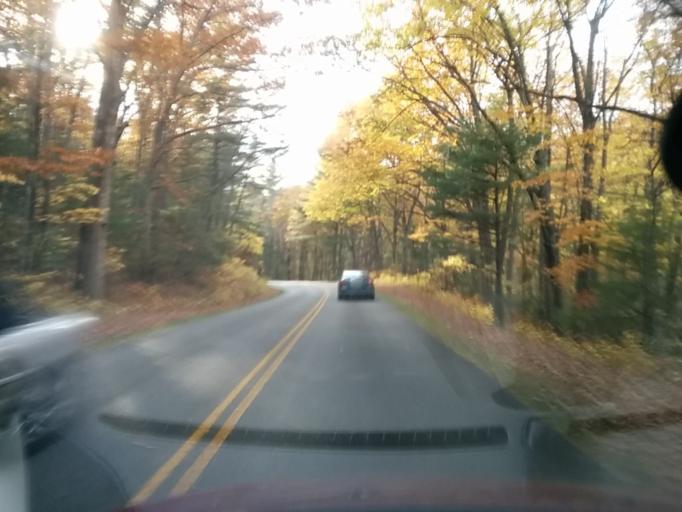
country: US
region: Virginia
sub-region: City of Buena Vista
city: Buena Vista
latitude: 37.7938
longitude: -79.2584
